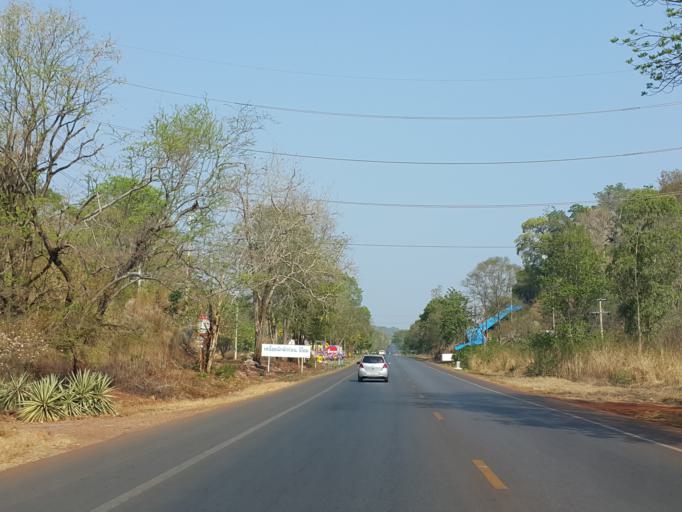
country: TH
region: Kanchanaburi
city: Sai Yok
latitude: 14.1015
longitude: 99.2285
